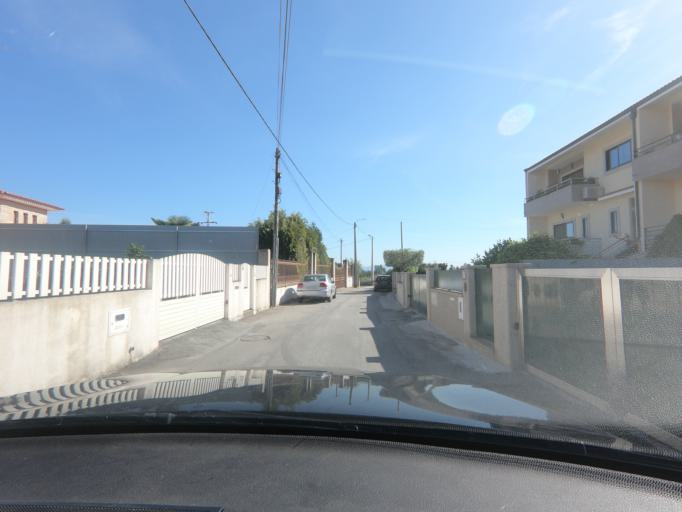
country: PT
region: Vila Real
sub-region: Vila Real
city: Vila Real
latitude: 41.2795
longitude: -7.7004
